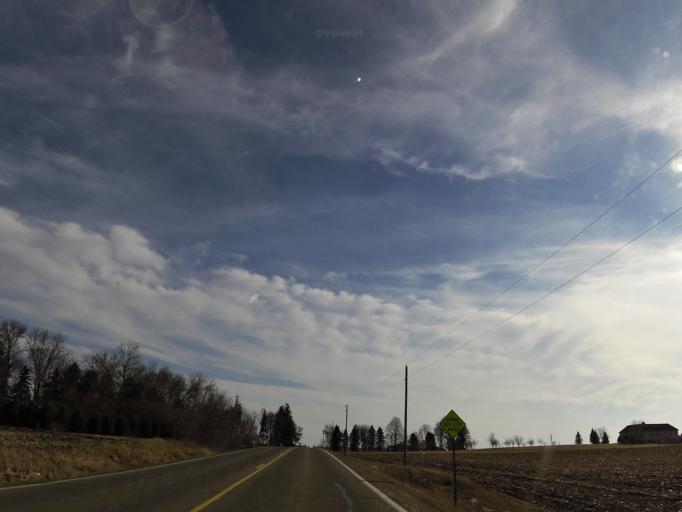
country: US
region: Minnesota
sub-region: Rice County
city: Northfield
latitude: 44.5319
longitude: -93.2011
